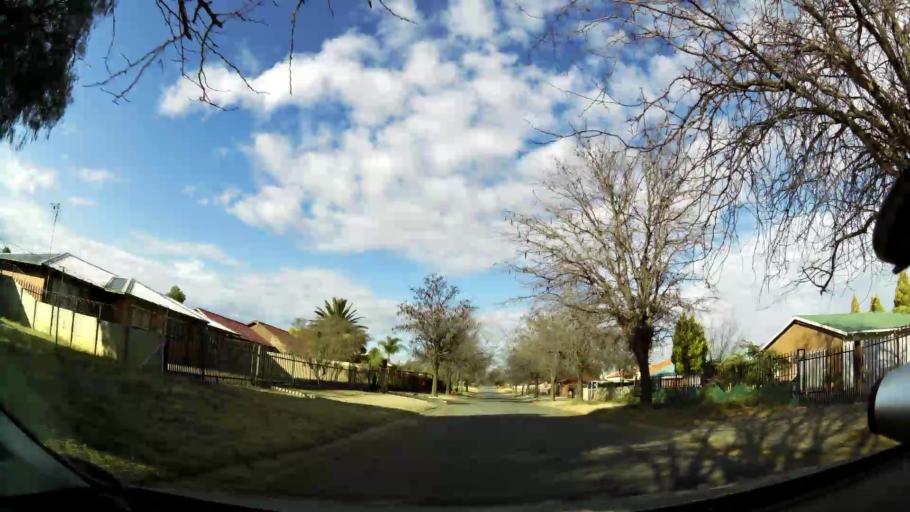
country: ZA
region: Orange Free State
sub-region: Lejweleputswa District Municipality
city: Welkom
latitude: -27.9800
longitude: 26.6997
